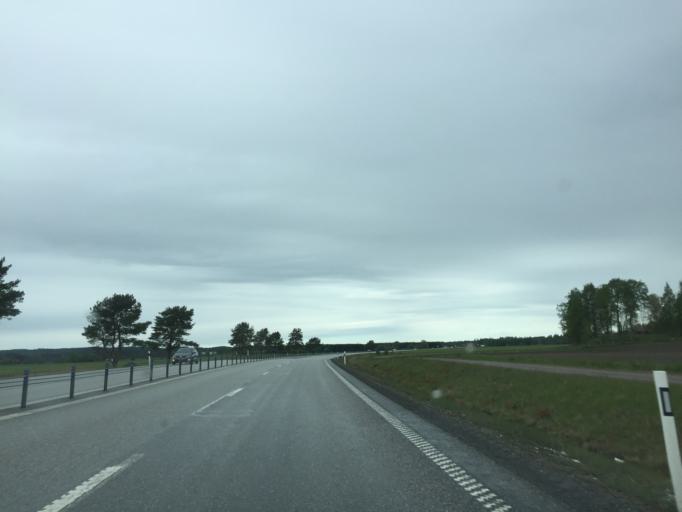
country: SE
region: OErebro
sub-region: Orebro Kommun
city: Hovsta
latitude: 59.4105
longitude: 15.1801
